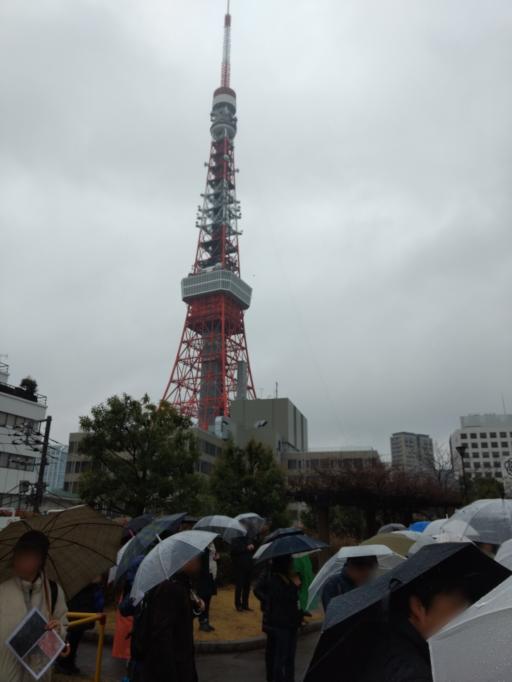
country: JP
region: Tokyo
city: Tokyo
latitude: 35.6608
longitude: 139.7455
